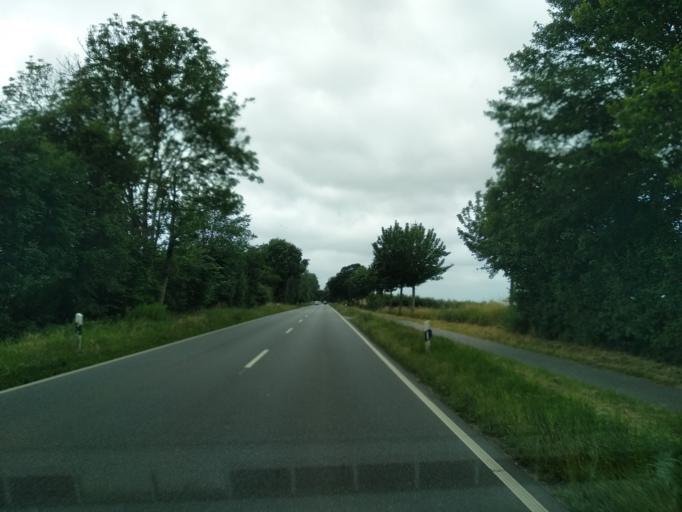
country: DE
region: Schleswig-Holstein
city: Ringsberg
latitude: 54.8024
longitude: 9.6138
